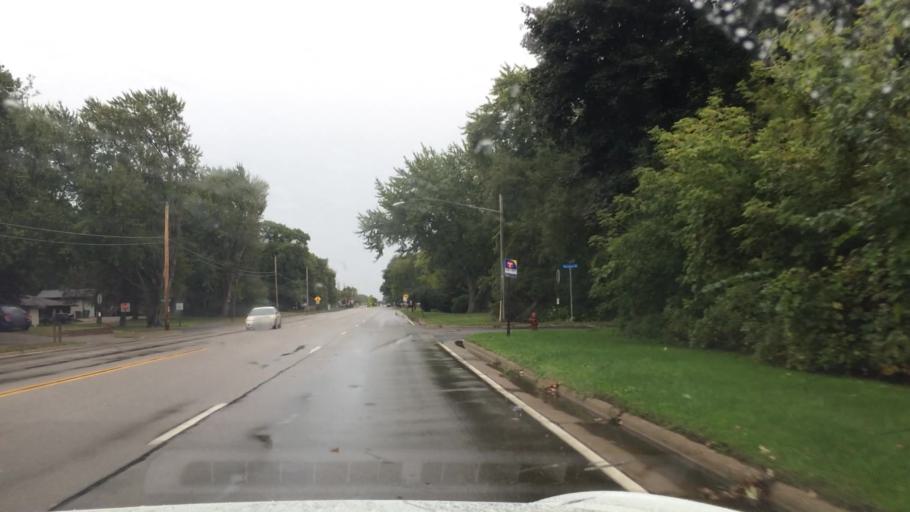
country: US
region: Minnesota
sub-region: Anoka County
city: Spring Lake Park
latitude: 45.1245
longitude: -93.2295
